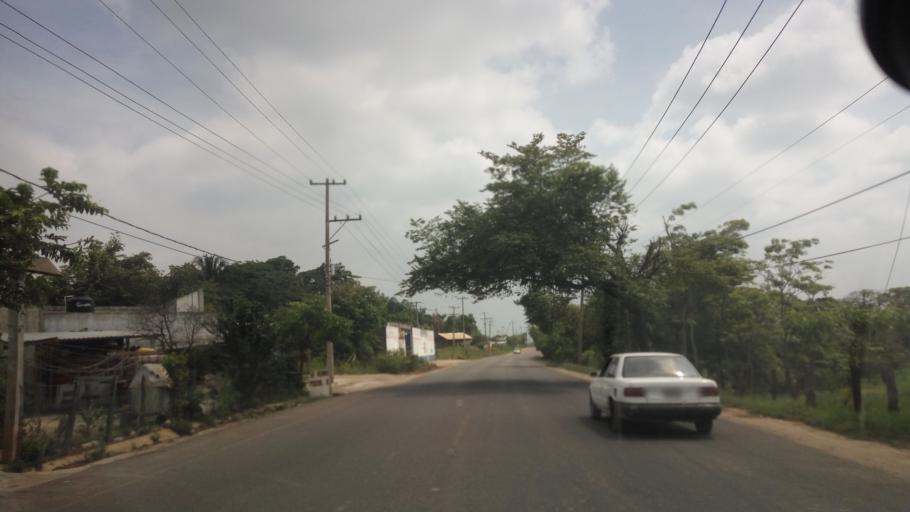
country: MX
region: Chiapas
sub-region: Reforma
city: El Carmen (El Limon)
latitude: 17.8783
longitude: -93.1508
